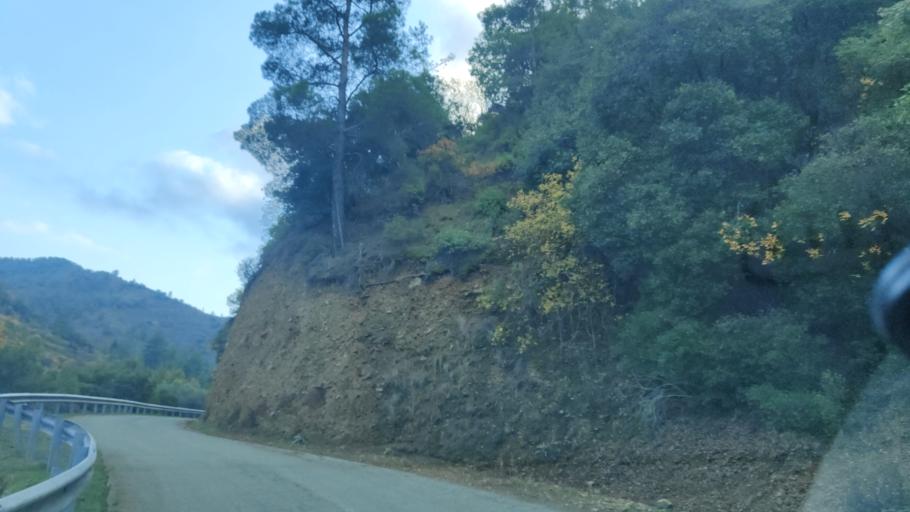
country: CY
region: Lefkosia
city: Lefka
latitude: 35.0486
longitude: 32.7357
